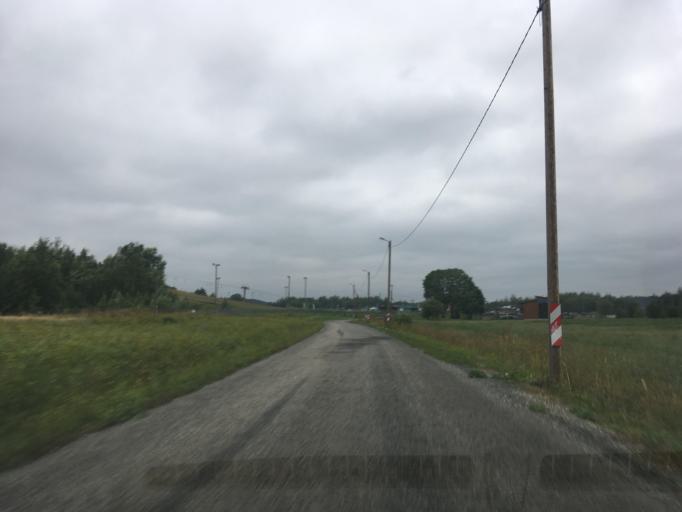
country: EE
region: Ida-Virumaa
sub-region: Kivioli linn
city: Kivioli
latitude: 59.3655
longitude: 26.9589
